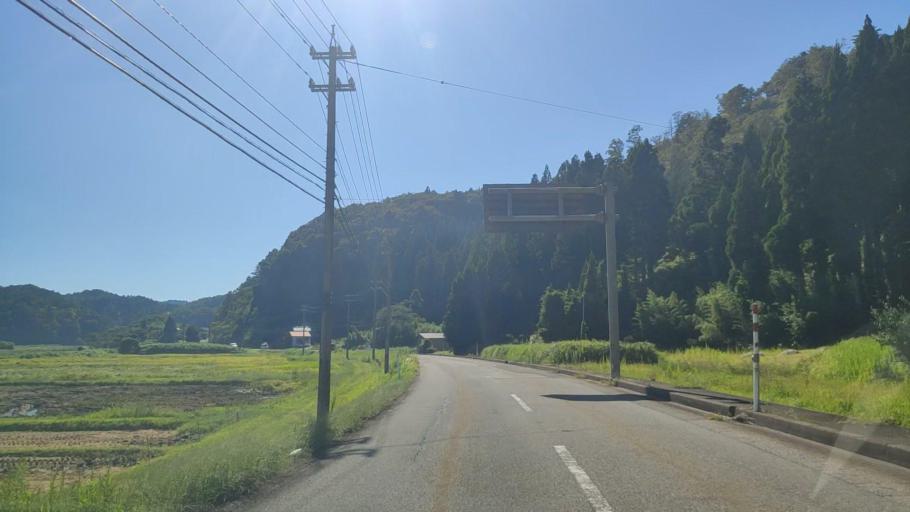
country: JP
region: Ishikawa
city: Nanao
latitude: 37.3405
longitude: 137.2190
